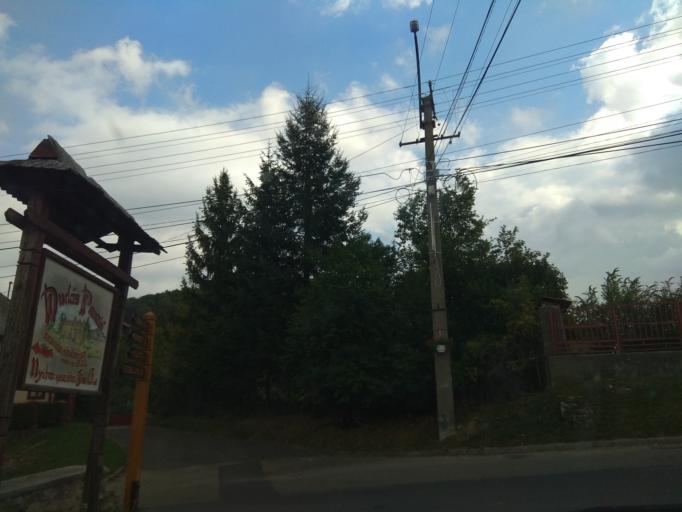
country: HU
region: Borsod-Abauj-Zemplen
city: Saly
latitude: 48.0680
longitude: 20.6338
